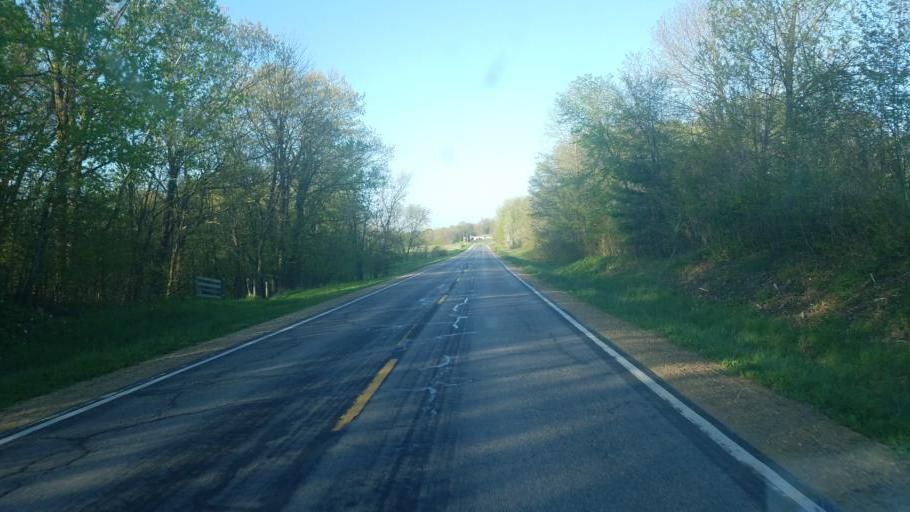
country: US
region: Wisconsin
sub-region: Vernon County
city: Hillsboro
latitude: 43.6048
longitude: -90.4674
